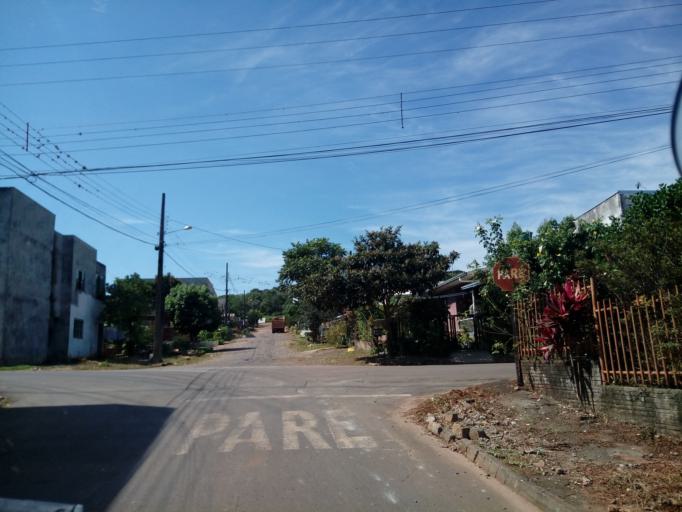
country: BR
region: Santa Catarina
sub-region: Chapeco
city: Chapeco
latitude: -27.1030
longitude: -52.6571
